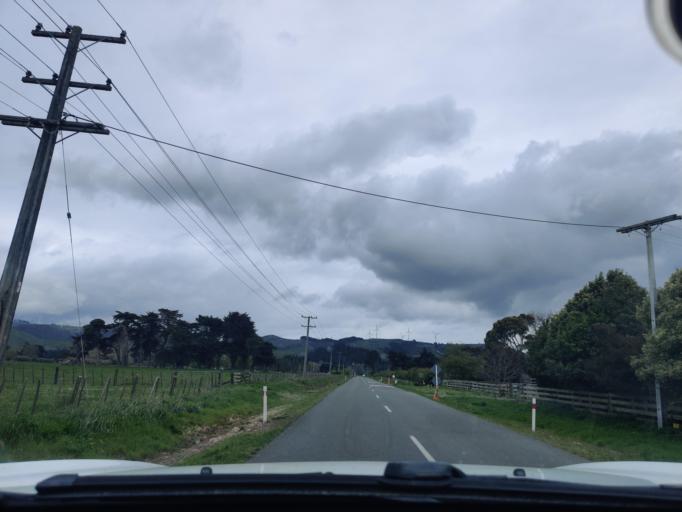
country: NZ
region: Manawatu-Wanganui
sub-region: Palmerston North City
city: Palmerston North
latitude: -40.3193
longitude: 175.8636
